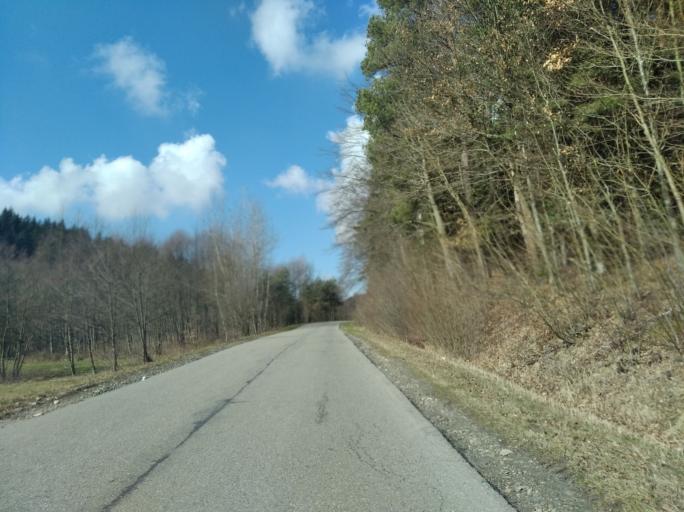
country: PL
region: Subcarpathian Voivodeship
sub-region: Powiat strzyzowski
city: Frysztak
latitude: 49.8651
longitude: 21.5446
